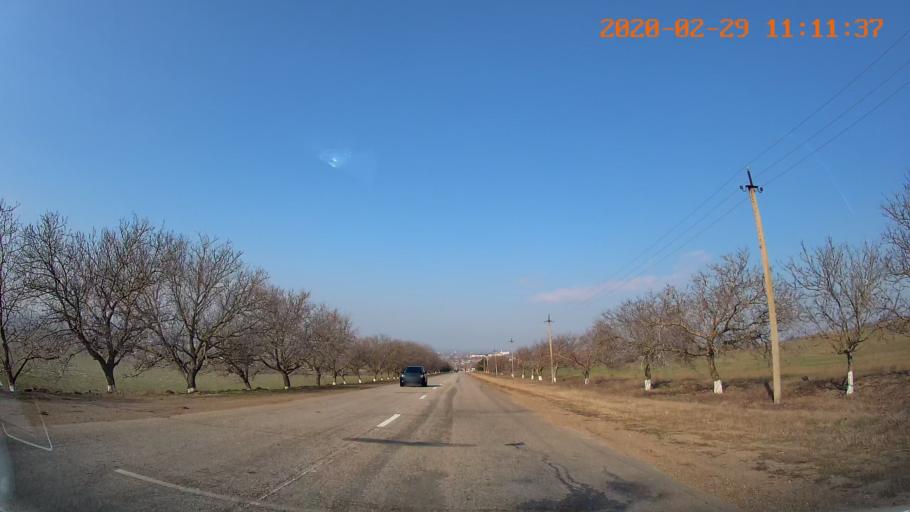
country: MD
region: Telenesti
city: Dubasari
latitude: 47.2568
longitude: 29.1949
